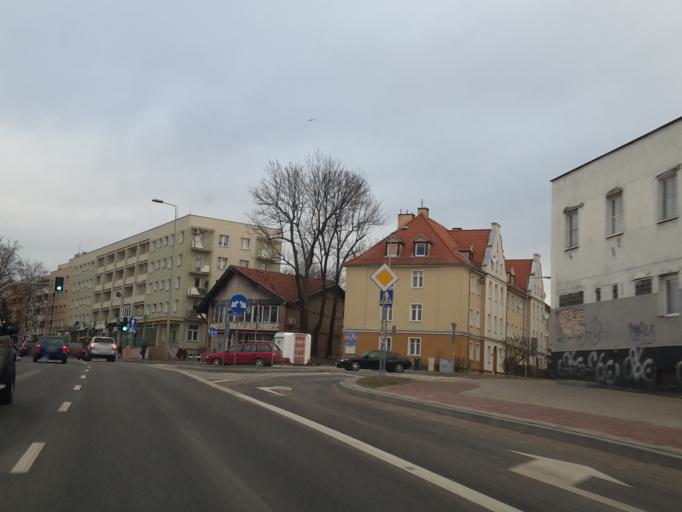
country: PL
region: Warmian-Masurian Voivodeship
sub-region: Powiat elblaski
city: Elblag
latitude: 54.1627
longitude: 19.4048
